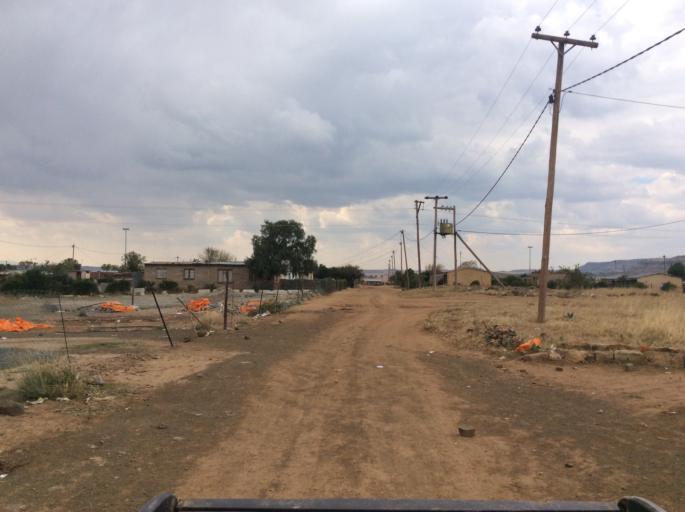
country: ZA
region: Orange Free State
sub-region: Xhariep District Municipality
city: Dewetsdorp
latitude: -29.5768
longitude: 26.6831
